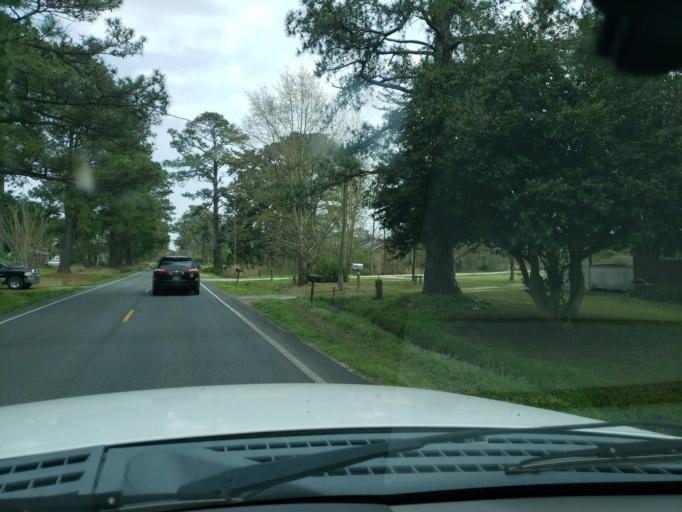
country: US
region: North Carolina
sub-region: Duplin County
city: Beulaville
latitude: 34.7753
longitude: -77.8167
